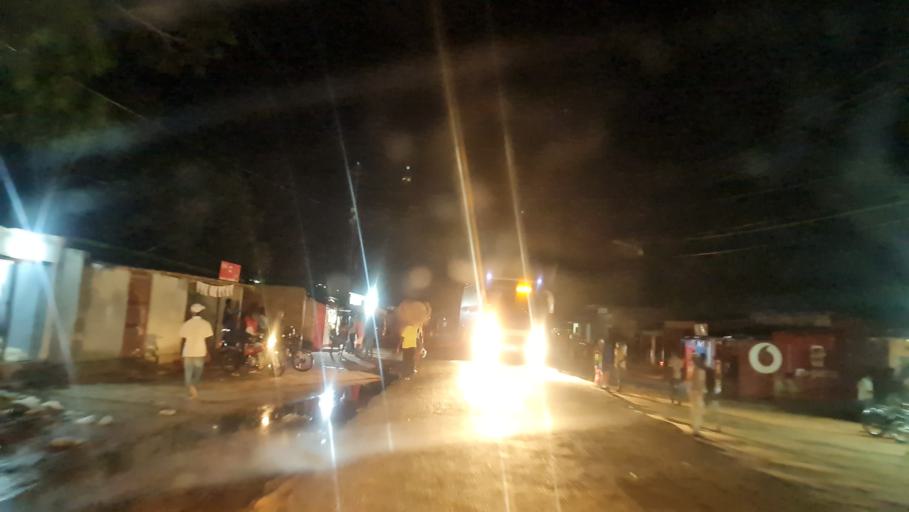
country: MZ
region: Nampula
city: Nacala
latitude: -14.6268
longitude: 40.6819
